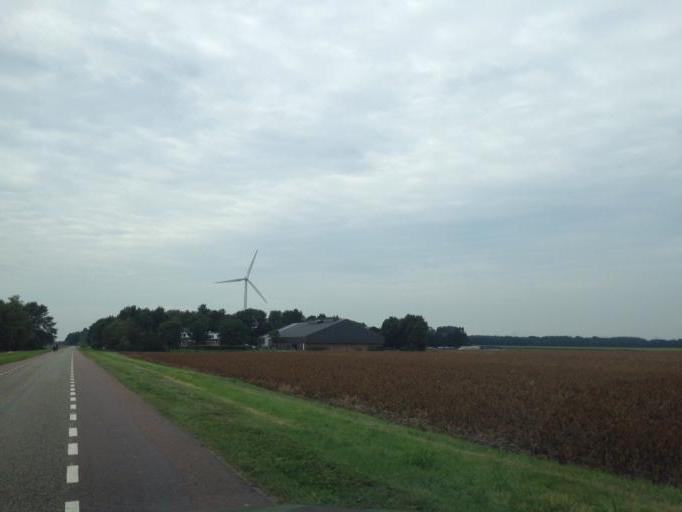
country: NL
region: Flevoland
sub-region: Gemeente Lelystad
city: Lelystad
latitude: 52.4129
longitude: 5.4125
